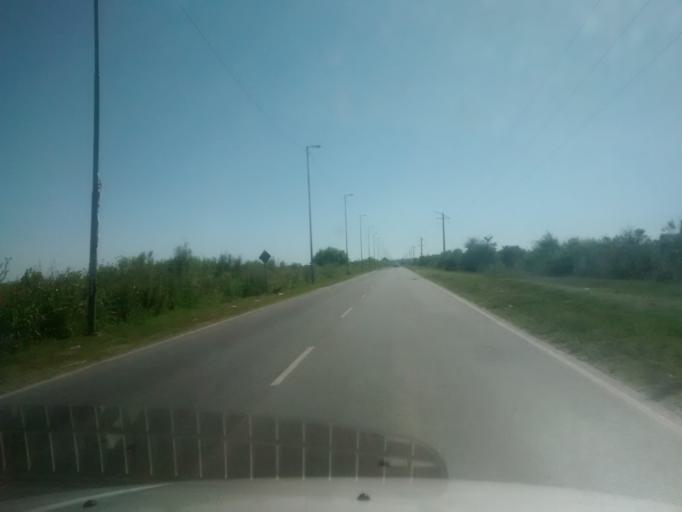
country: AR
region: Buenos Aires
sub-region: Partido de Berisso
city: Berisso
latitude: -34.8949
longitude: -57.8801
